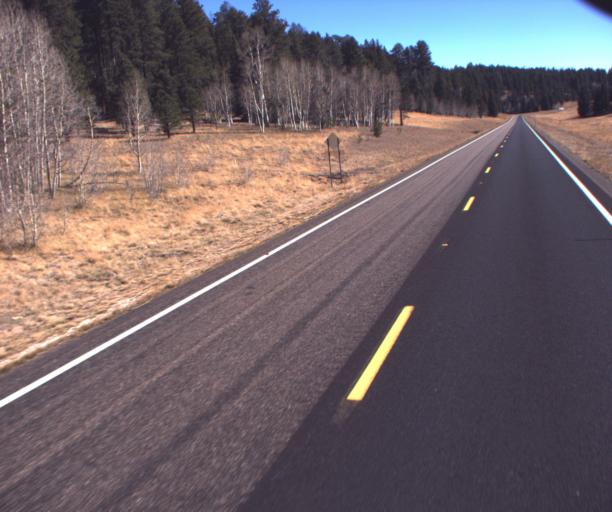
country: US
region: Arizona
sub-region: Coconino County
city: Grand Canyon
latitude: 36.5427
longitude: -112.1666
